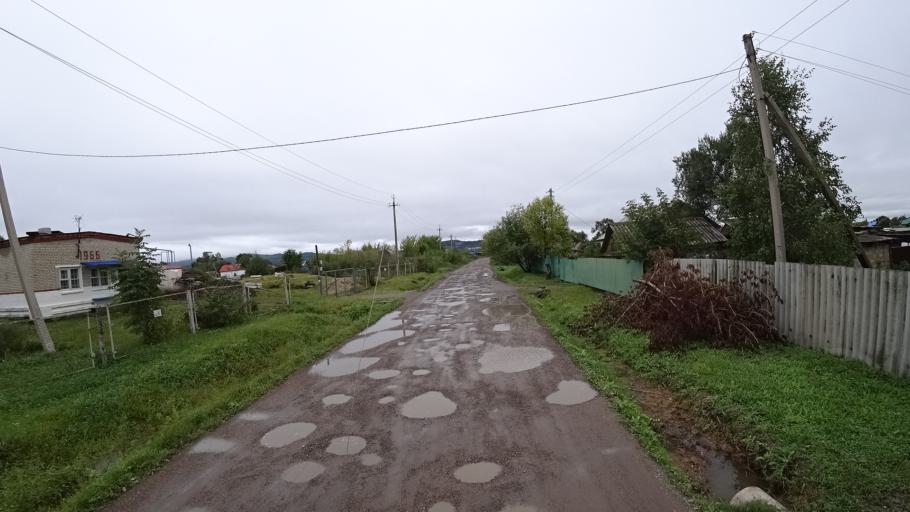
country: RU
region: Primorskiy
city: Monastyrishche
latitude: 44.1974
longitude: 132.4620
